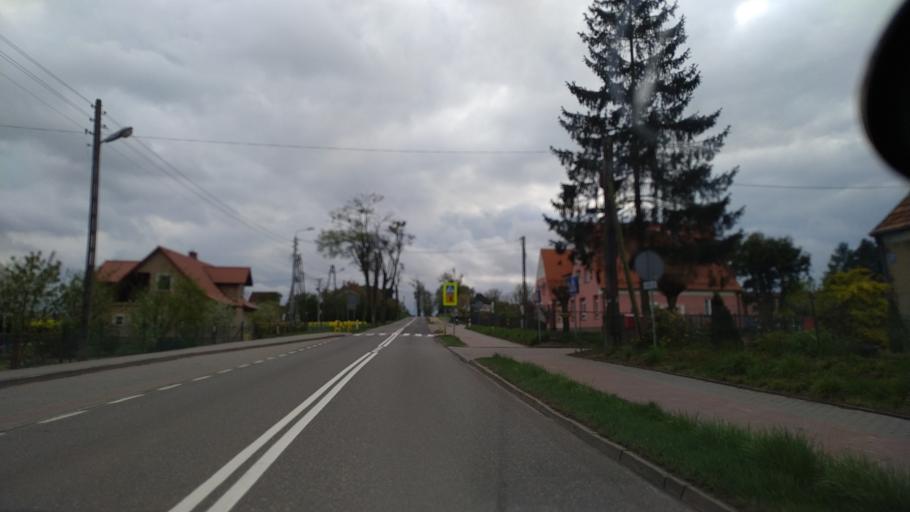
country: PL
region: Pomeranian Voivodeship
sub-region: Powiat kwidzynski
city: Ryjewo
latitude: 53.7856
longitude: 18.9632
